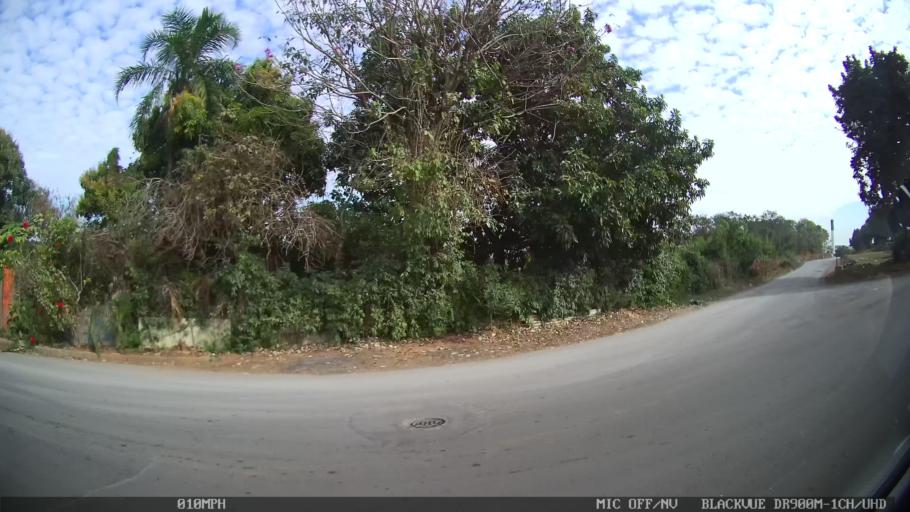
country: BR
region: Sao Paulo
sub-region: Santa Barbara D'Oeste
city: Santa Barbara d'Oeste
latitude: -22.7696
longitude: -47.3970
